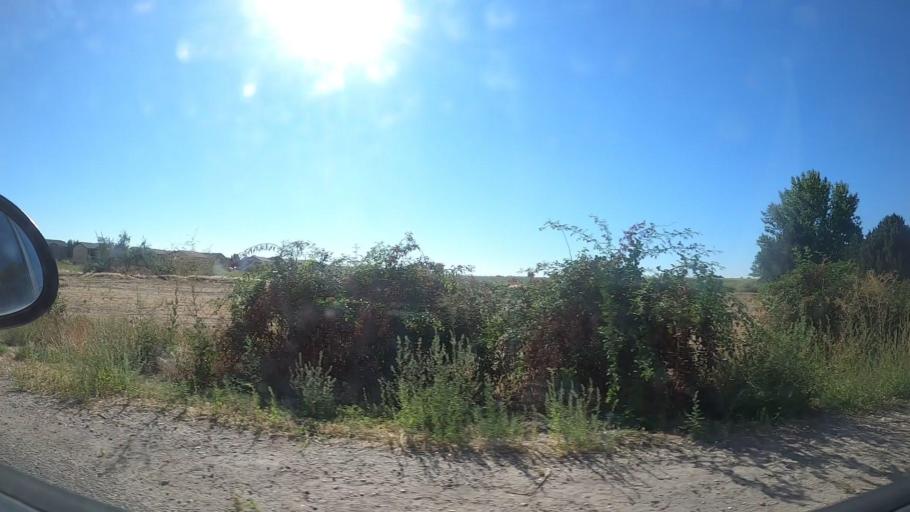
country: US
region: Idaho
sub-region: Canyon County
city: Nampa
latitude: 43.6031
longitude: -116.6133
